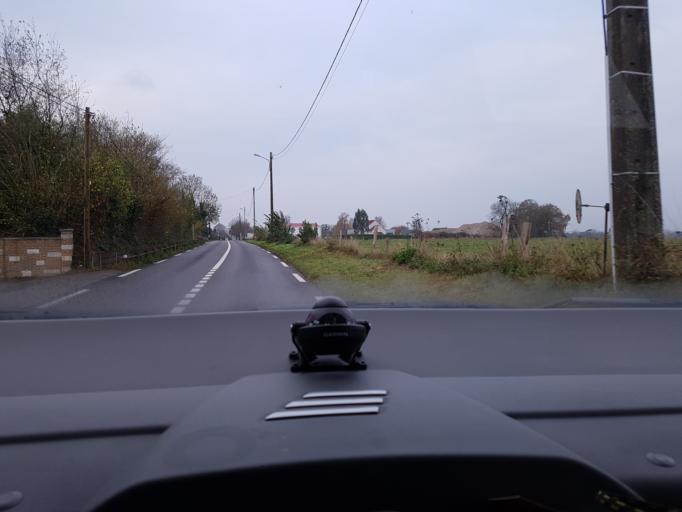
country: FR
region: Haute-Normandie
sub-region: Departement de la Seine-Maritime
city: Roumare
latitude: 49.4999
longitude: 0.9591
